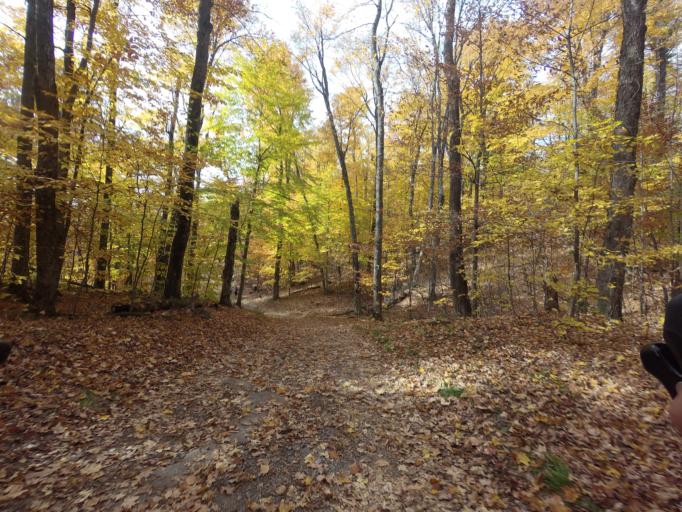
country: CA
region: Quebec
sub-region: Outaouais
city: Gatineau
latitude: 45.5027
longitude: -75.8668
